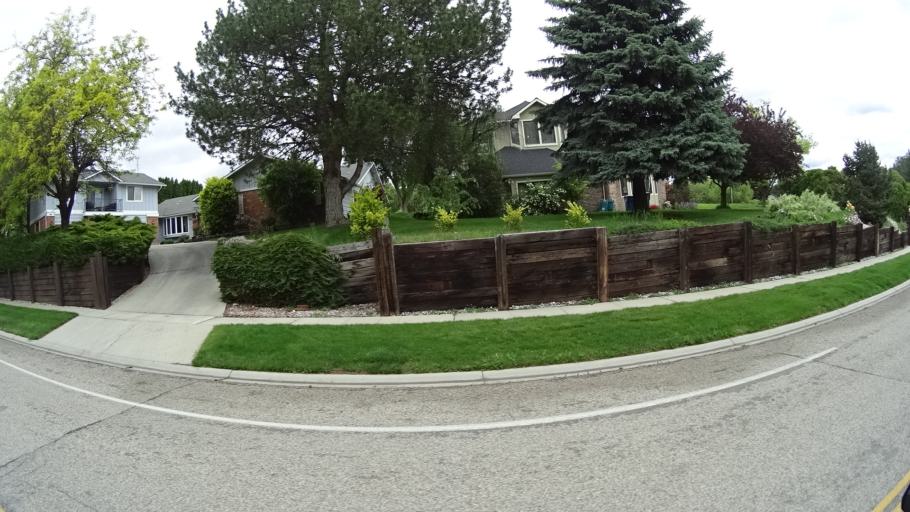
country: US
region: Idaho
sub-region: Ada County
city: Eagle
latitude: 43.7021
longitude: -116.3431
